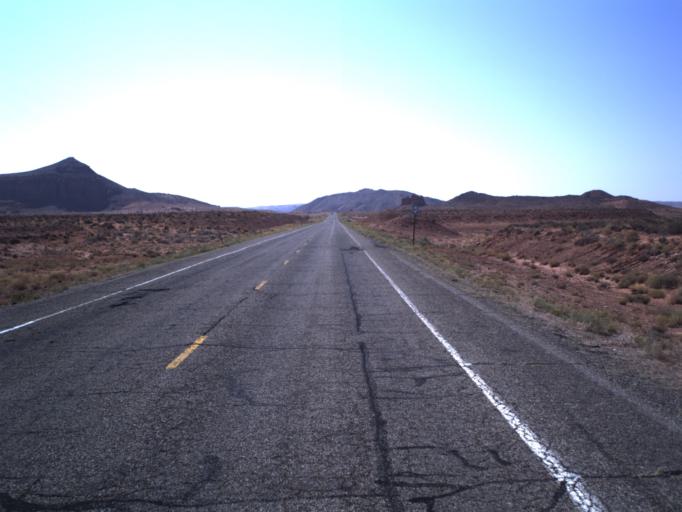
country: US
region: Utah
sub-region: San Juan County
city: Blanding
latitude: 36.9983
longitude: -109.6091
